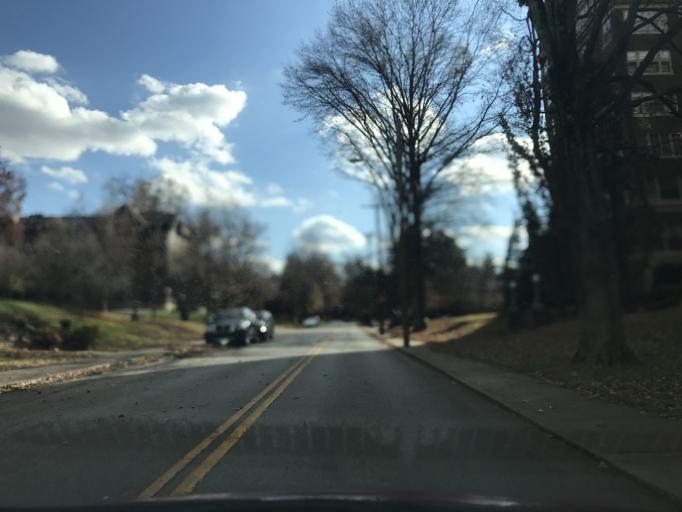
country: US
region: Kentucky
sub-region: Jefferson County
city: Audubon Park
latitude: 38.2349
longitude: -85.7085
